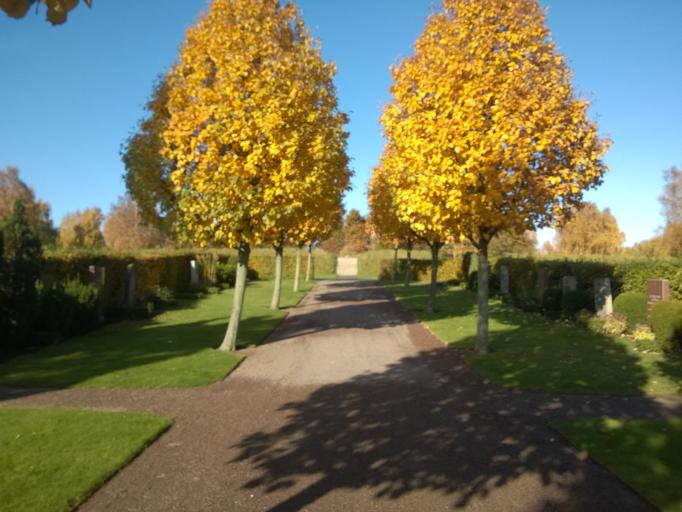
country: SE
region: Skane
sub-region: Malmo
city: Malmoe
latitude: 55.5935
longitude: 13.0445
